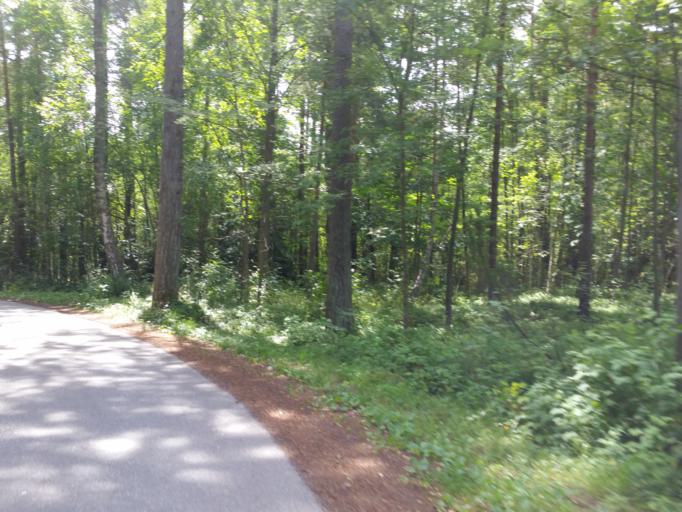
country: FI
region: Uusimaa
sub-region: Raaseporin
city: Hanko
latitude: 59.8432
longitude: 22.9421
